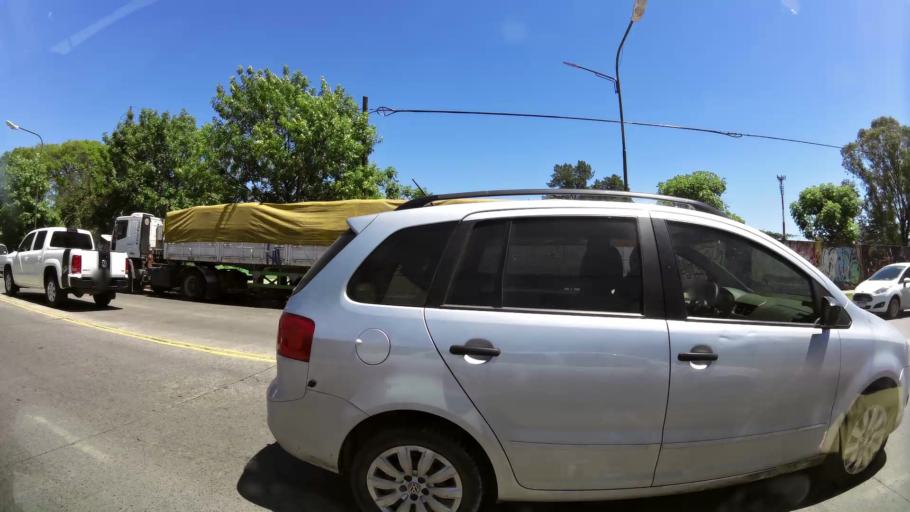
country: AR
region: Buenos Aires
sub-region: Partido de San Isidro
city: San Isidro
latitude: -34.5065
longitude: -58.5642
